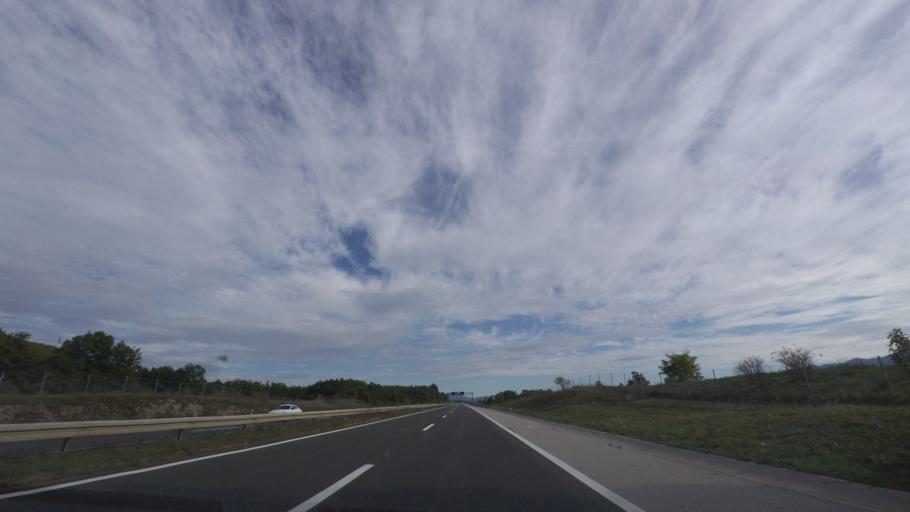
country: HR
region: Zadarska
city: Starigrad
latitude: 44.4339
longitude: 15.6264
